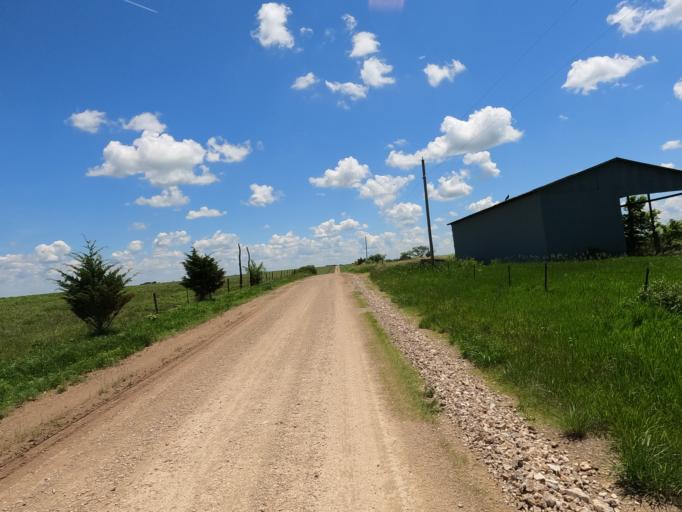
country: US
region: Kansas
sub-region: Chase County
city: Cottonwood Falls
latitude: 38.2169
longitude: -96.7340
